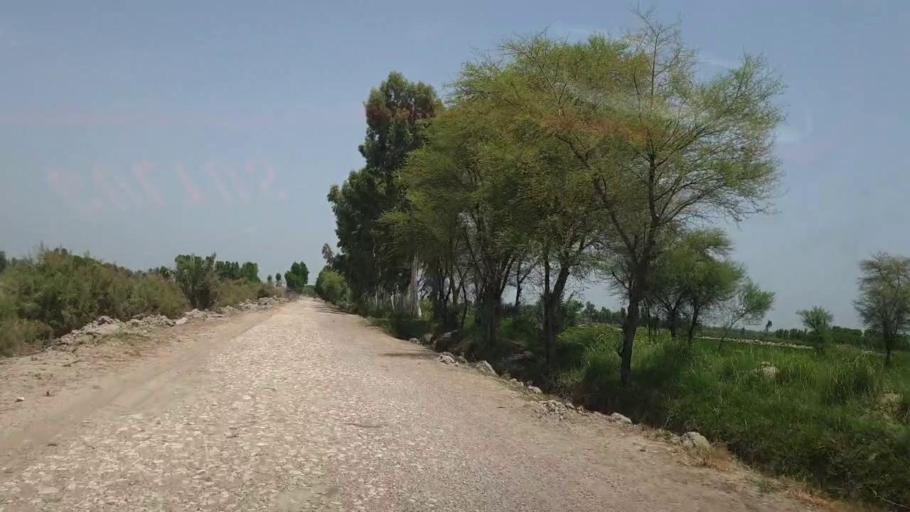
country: PK
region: Sindh
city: Daulatpur
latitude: 26.4882
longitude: 68.1346
